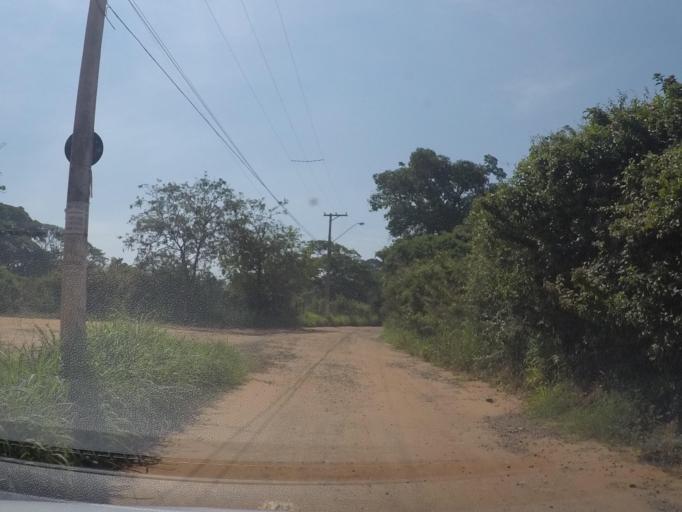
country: BR
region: Sao Paulo
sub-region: Monte Mor
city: Monte Mor
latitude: -22.8859
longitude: -47.3015
